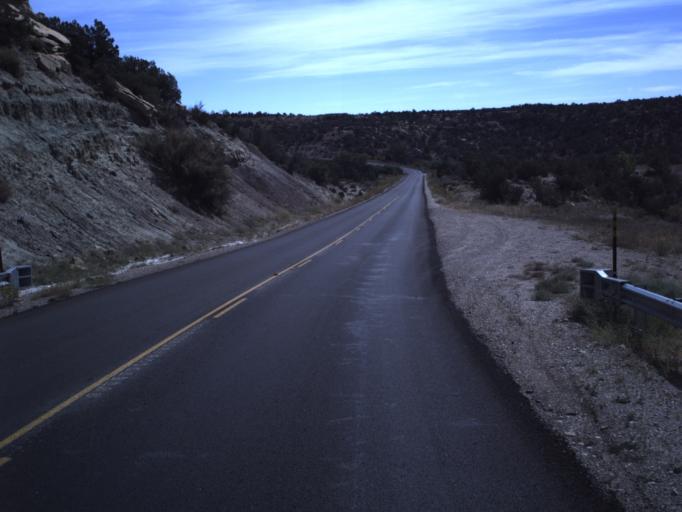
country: US
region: Utah
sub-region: San Juan County
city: Blanding
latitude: 37.5782
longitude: -109.5126
